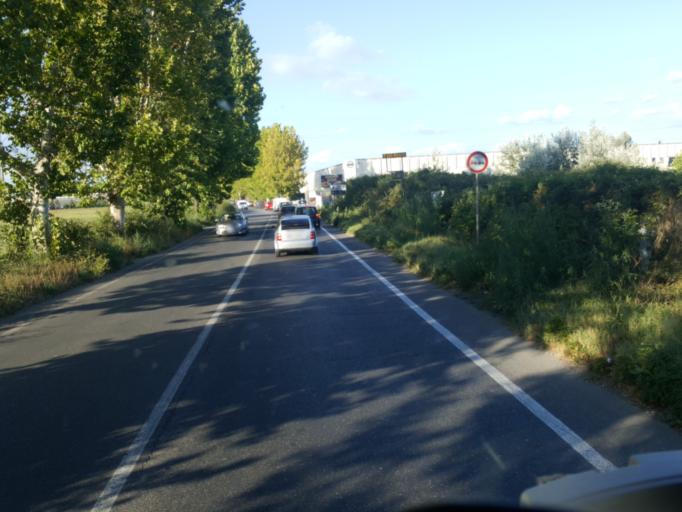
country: IT
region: Latium
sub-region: Citta metropolitana di Roma Capitale
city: Girardi-Bellavista-Terrazze
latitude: 42.1105
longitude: 12.5850
